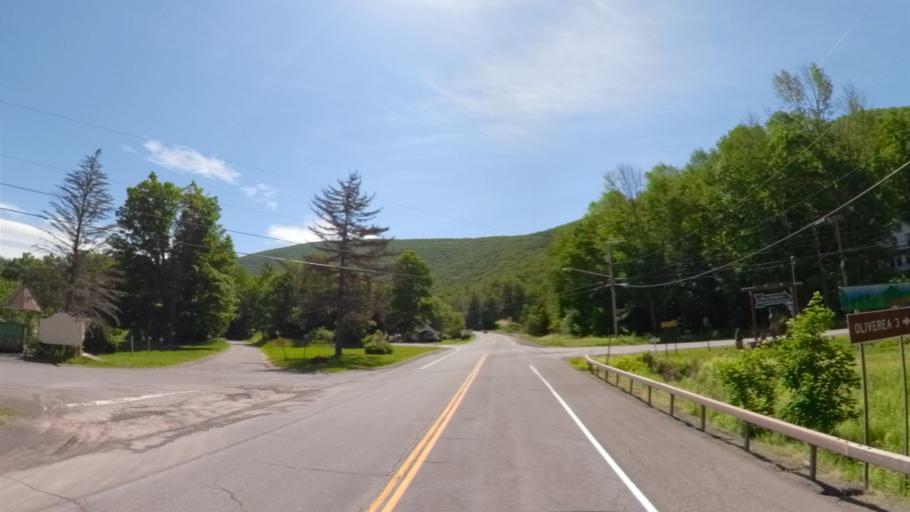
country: US
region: New York
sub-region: Ulster County
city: Shokan
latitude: 42.1030
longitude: -74.4439
